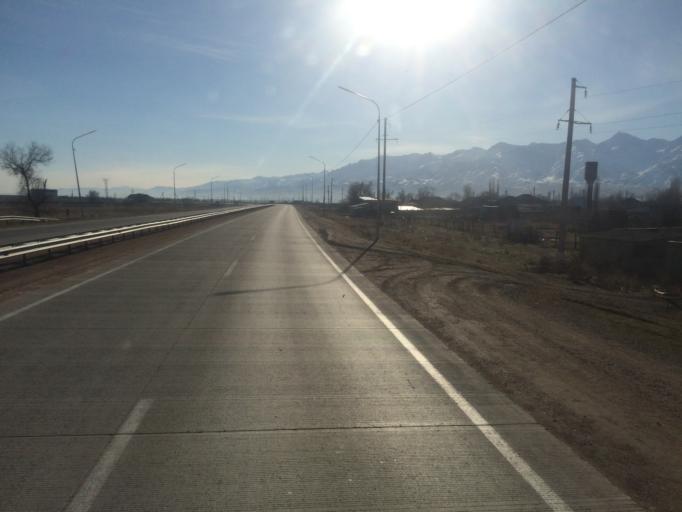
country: KG
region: Talas
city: Ivanovo-Alekseyevka
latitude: 42.9938
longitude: 72.1101
